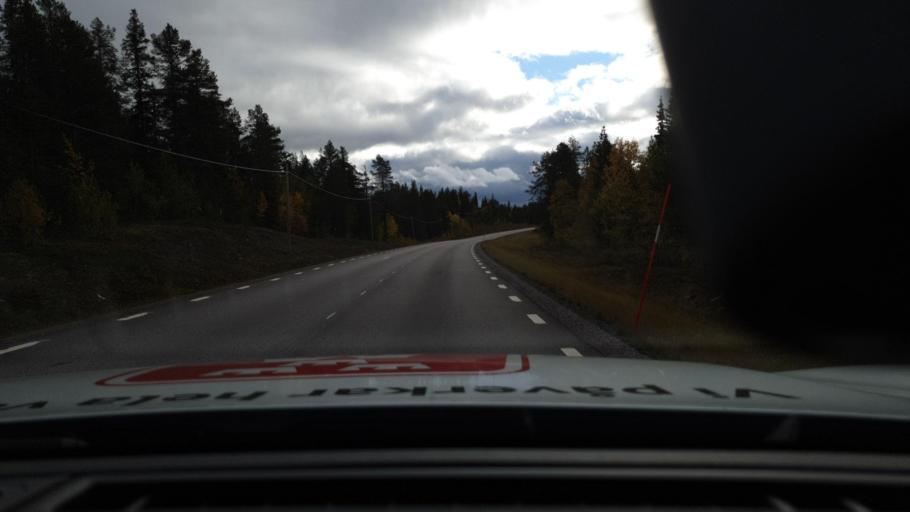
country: SE
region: Norrbotten
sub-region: Gallivare Kommun
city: Malmberget
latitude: 67.3974
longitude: 21.1108
